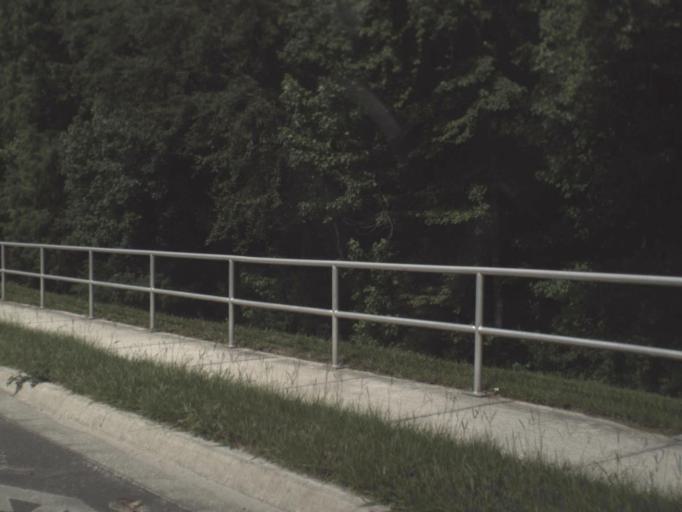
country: US
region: Florida
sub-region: Baker County
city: Macclenny
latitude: 30.2696
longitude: -82.1225
